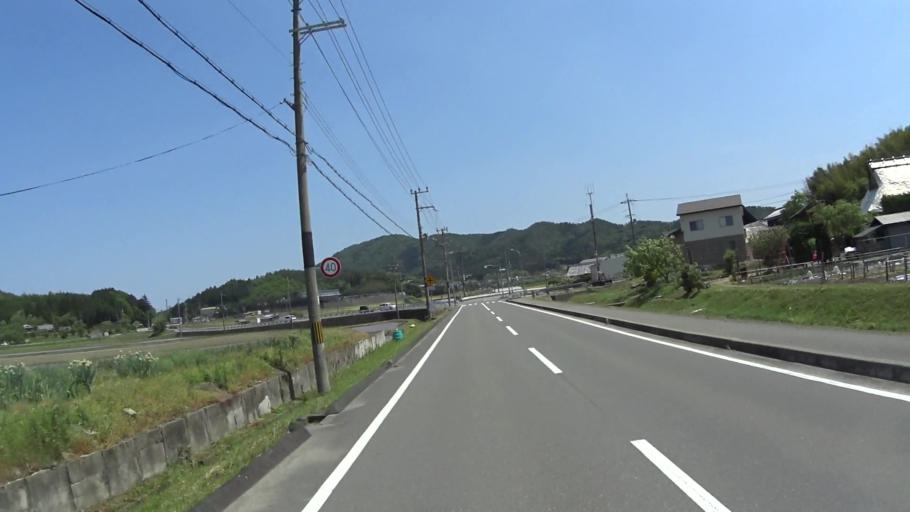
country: JP
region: Kyoto
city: Kameoka
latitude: 35.0261
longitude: 135.4871
